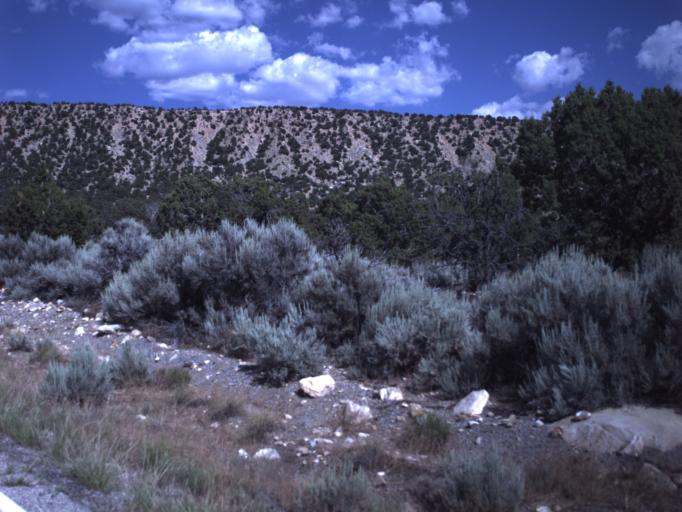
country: US
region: Utah
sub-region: Carbon County
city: Helper
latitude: 39.6764
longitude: -110.8146
